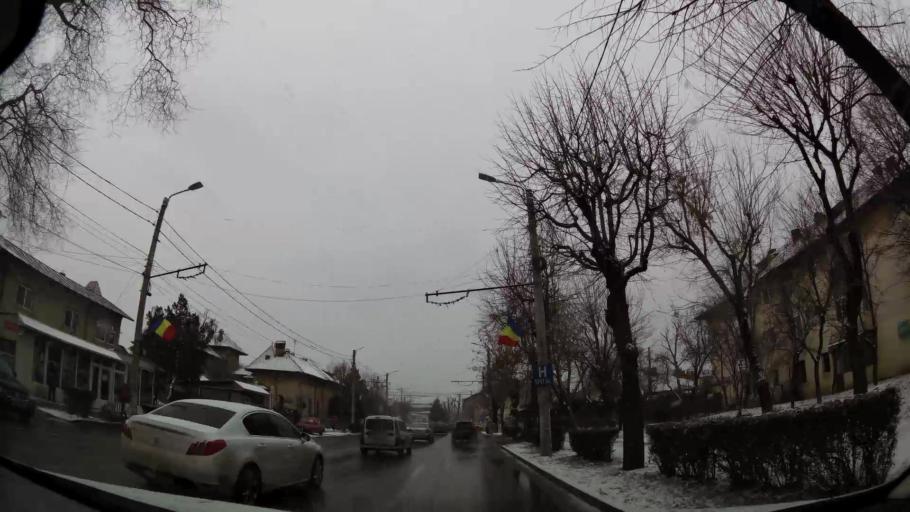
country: RO
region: Dambovita
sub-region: Municipiul Targoviste
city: Targoviste
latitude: 44.9201
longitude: 25.4576
